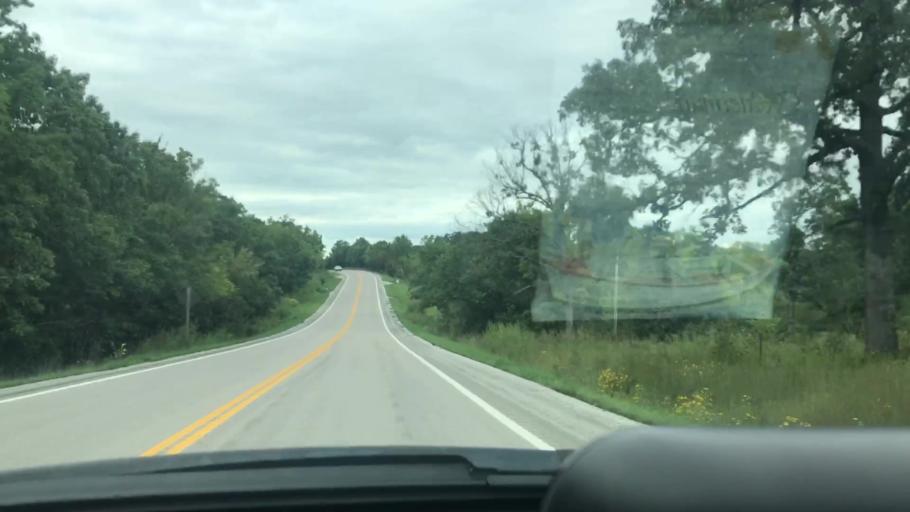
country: US
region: Missouri
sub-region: Benton County
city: Warsaw
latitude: 38.1668
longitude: -93.3088
